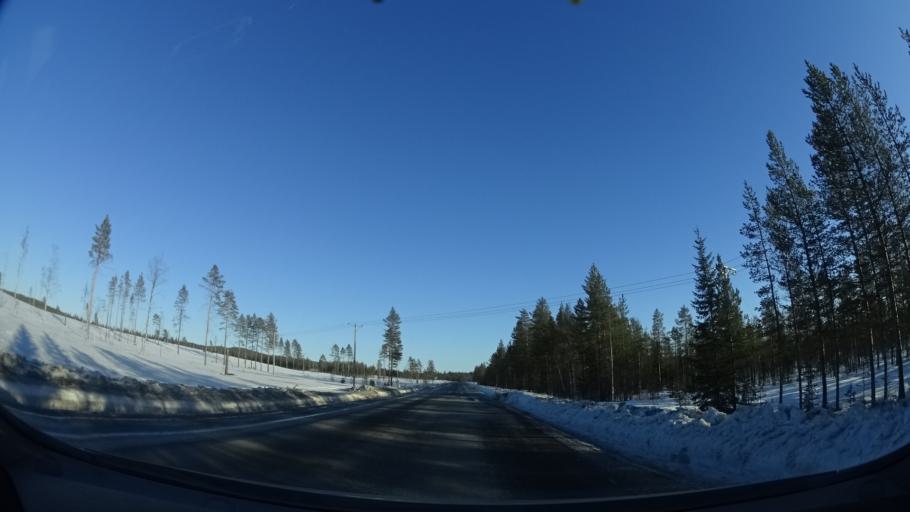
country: SE
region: Vaesterbotten
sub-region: Skelleftea Kommun
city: Langsele
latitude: 65.0364
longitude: 20.0932
